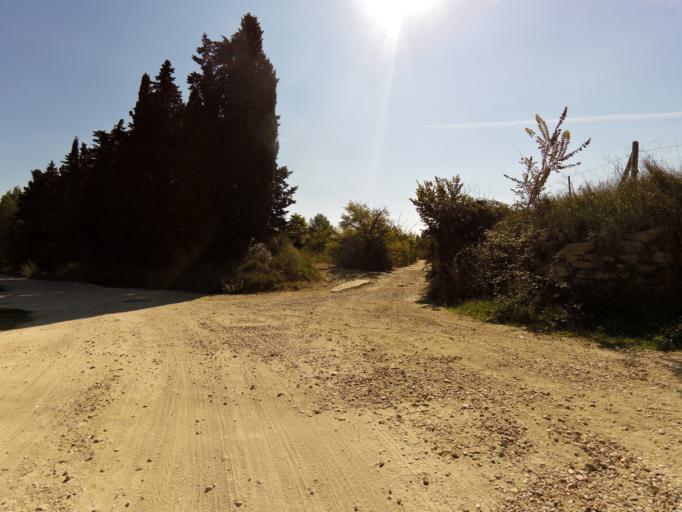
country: FR
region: Languedoc-Roussillon
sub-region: Departement du Gard
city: Aigues-Vives
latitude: 43.7322
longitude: 4.1698
